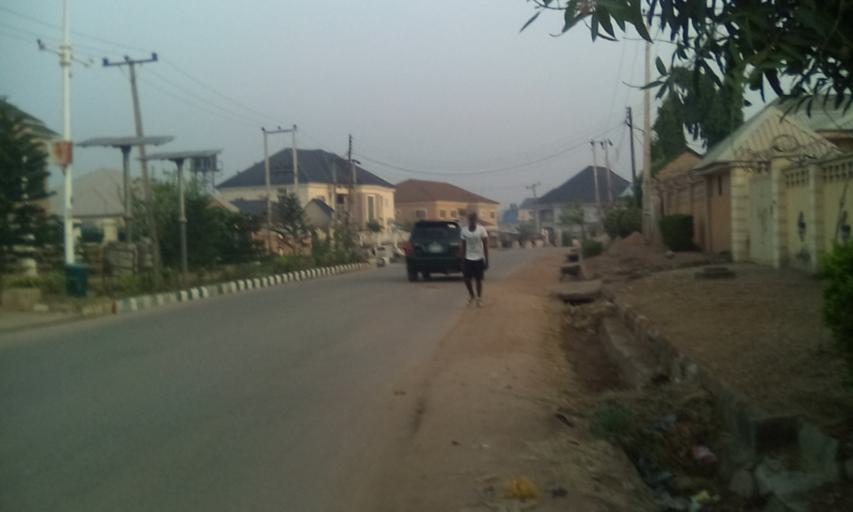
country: NG
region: Abuja Federal Capital Territory
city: Abuja
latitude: 8.9846
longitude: 7.3539
